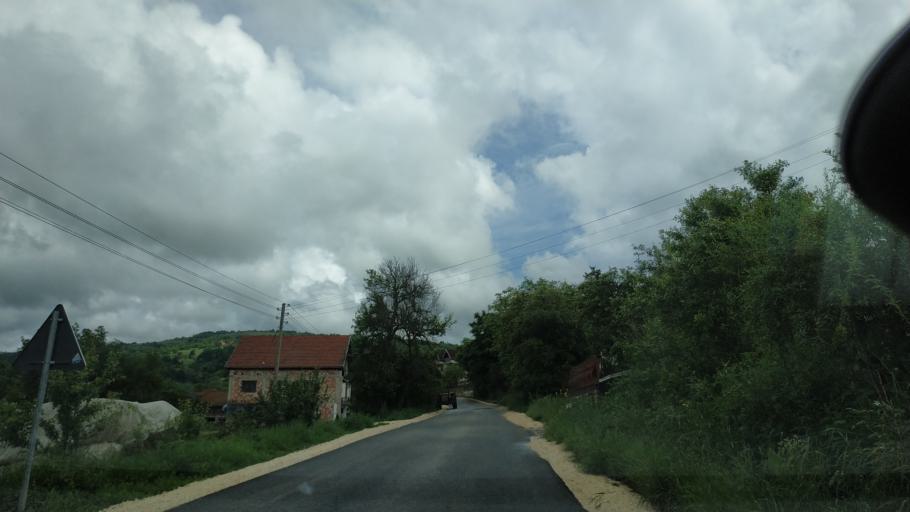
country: RS
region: Central Serbia
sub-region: Zajecarski Okrug
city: Soko Banja
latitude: 43.6744
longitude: 21.9133
